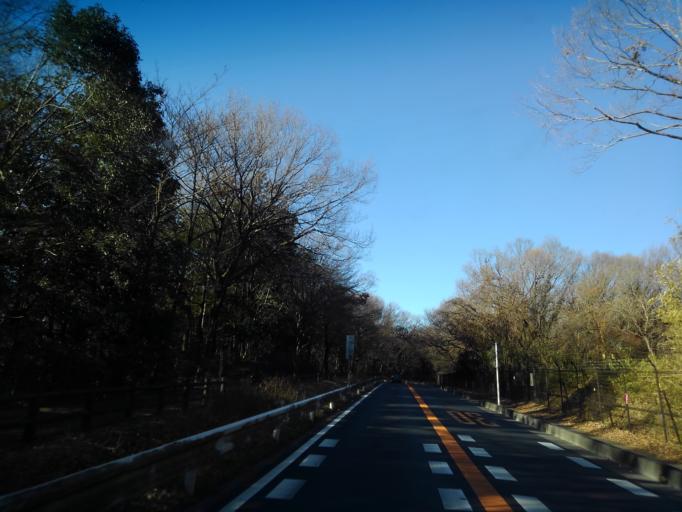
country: JP
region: Tokyo
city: Higashimurayama-shi
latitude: 35.7689
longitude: 139.4084
